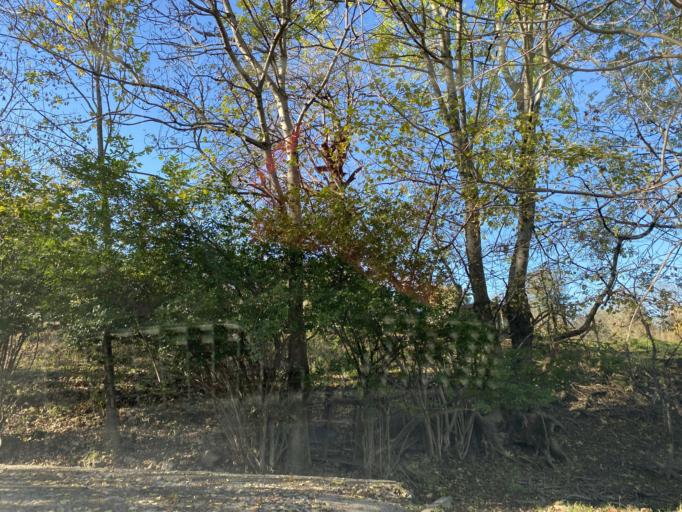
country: IT
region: Lombardy
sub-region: Provincia di Como
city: Pellio Intelvi
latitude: 45.9745
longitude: 9.0573
